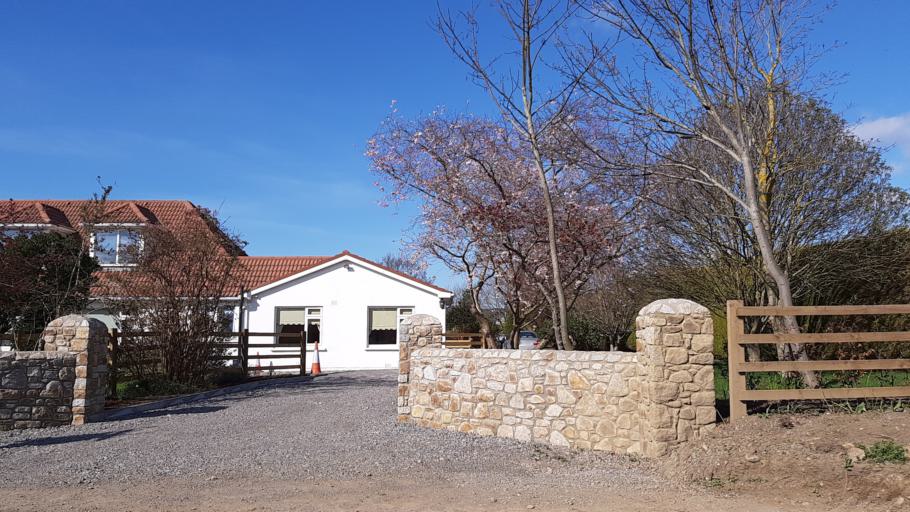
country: IE
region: Leinster
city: Malahide
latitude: 53.4339
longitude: -6.1672
